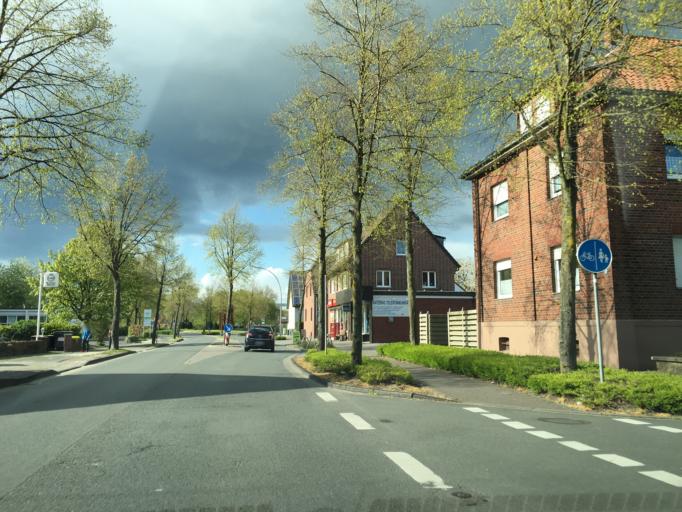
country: DE
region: North Rhine-Westphalia
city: Ludinghausen
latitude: 51.7705
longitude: 7.4584
